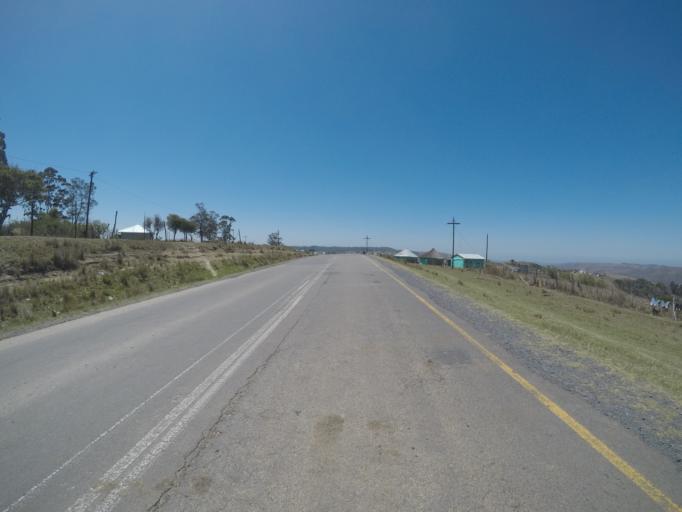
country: ZA
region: Eastern Cape
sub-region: OR Tambo District Municipality
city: Mthatha
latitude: -31.8976
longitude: 28.9376
